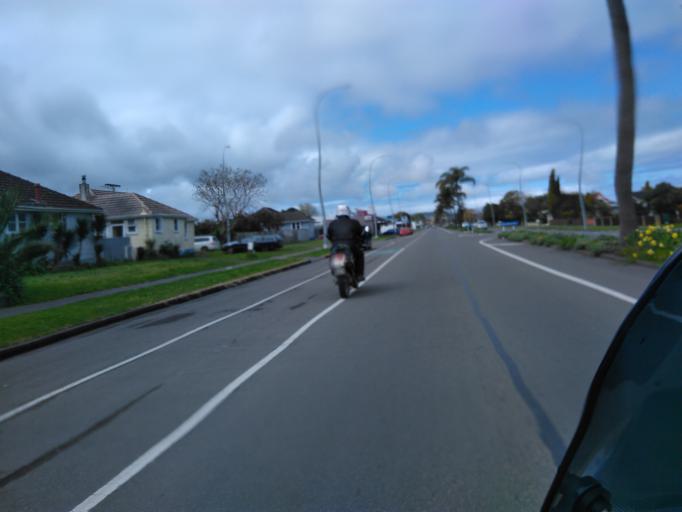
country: NZ
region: Gisborne
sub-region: Gisborne District
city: Gisborne
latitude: -38.6532
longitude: 178.0022
